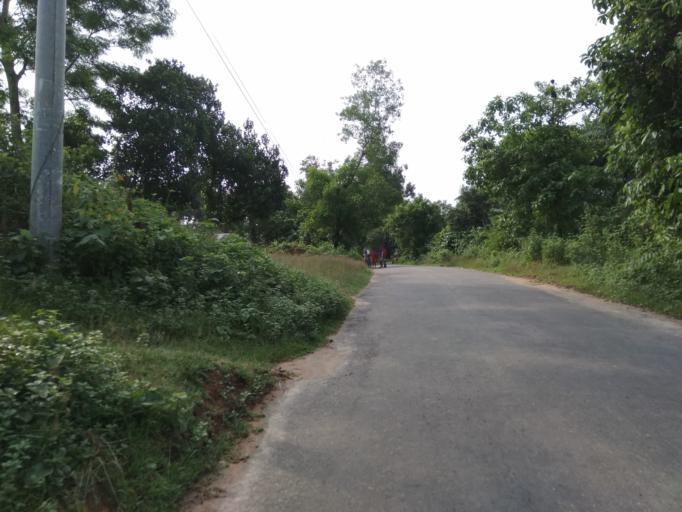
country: BD
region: Chittagong
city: Khagrachhari
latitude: 23.0318
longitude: 92.0103
